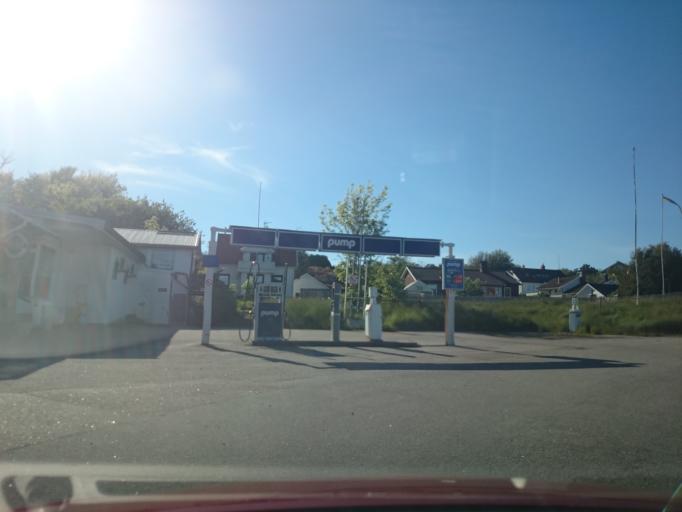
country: SE
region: Vaestra Goetaland
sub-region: Lysekils Kommun
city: Lysekil
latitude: 58.2388
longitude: 11.4571
